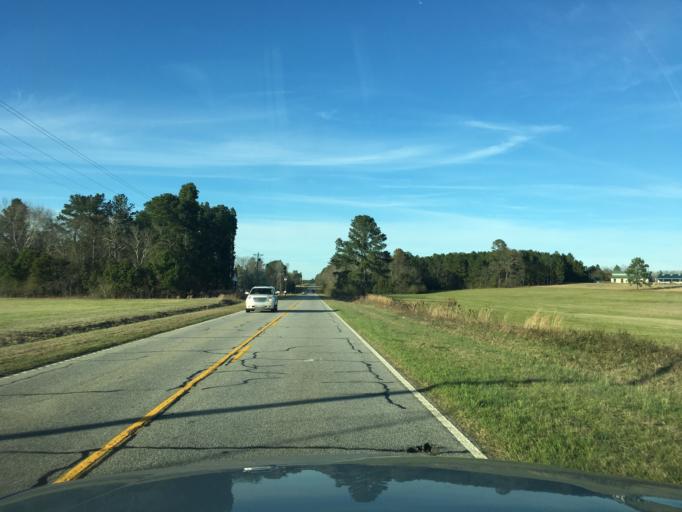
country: US
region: South Carolina
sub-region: Edgefield County
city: Johnston
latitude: 33.7609
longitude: -81.6423
